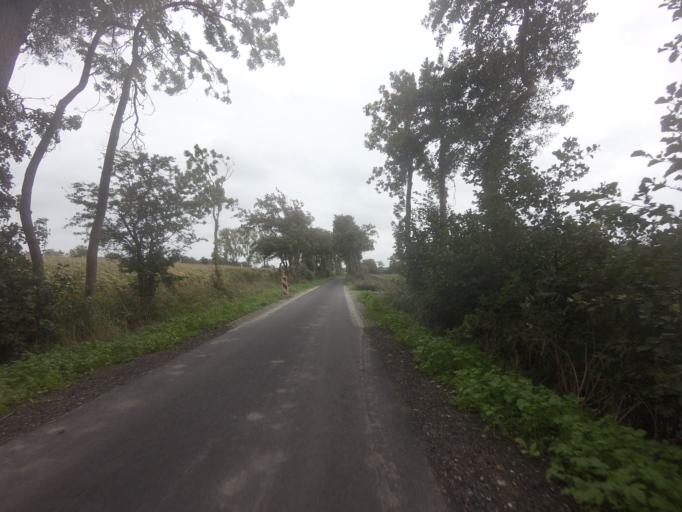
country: NL
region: Friesland
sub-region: Gemeente Leeuwarderadeel
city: Britsum
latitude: 53.2328
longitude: 5.7809
